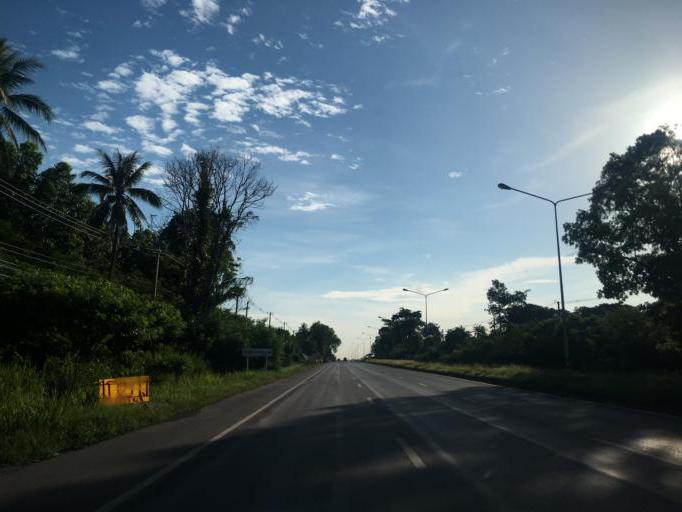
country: TH
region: Changwat Udon Thani
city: Kut Chap
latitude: 17.3280
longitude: 102.6531
